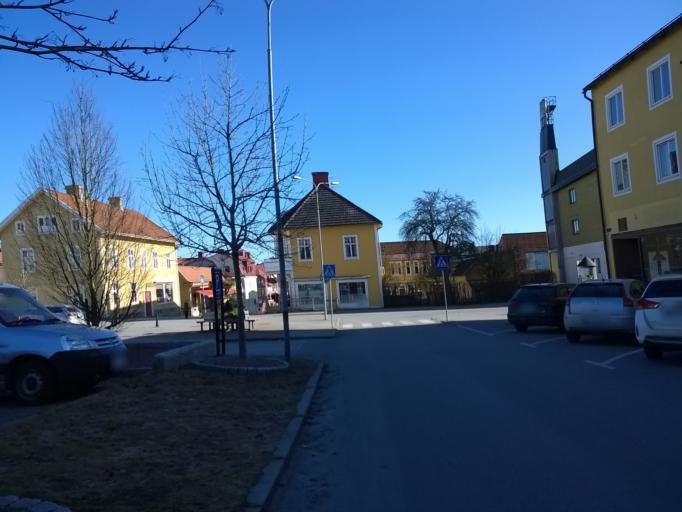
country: SE
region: Kronoberg
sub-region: Alvesta Kommun
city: Alvesta
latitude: 56.9009
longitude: 14.5549
